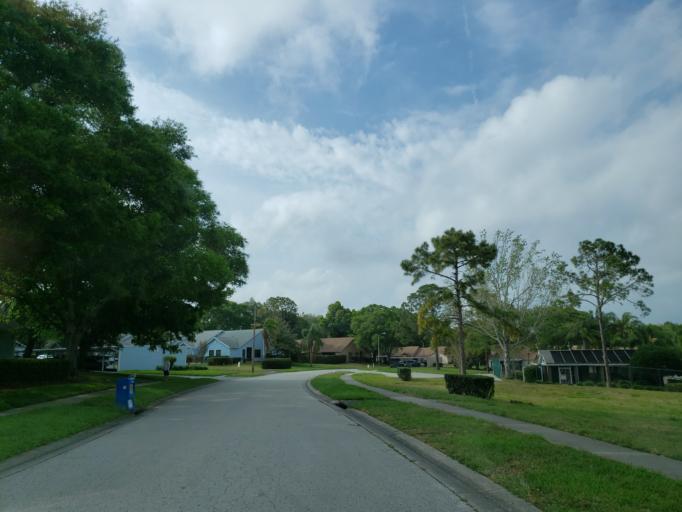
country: US
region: Florida
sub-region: Pinellas County
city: Saint George
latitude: 28.0905
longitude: -82.7300
